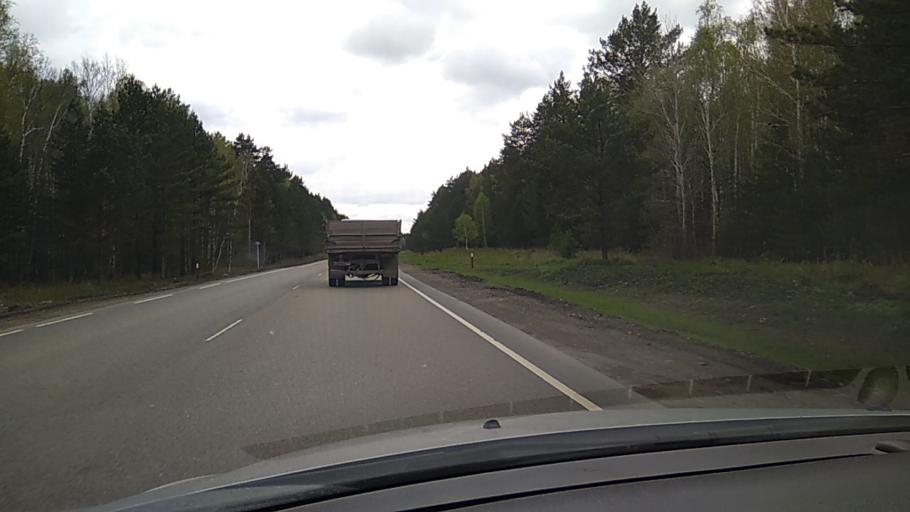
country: RU
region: Kurgan
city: Kataysk
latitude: 56.2987
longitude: 62.3806
